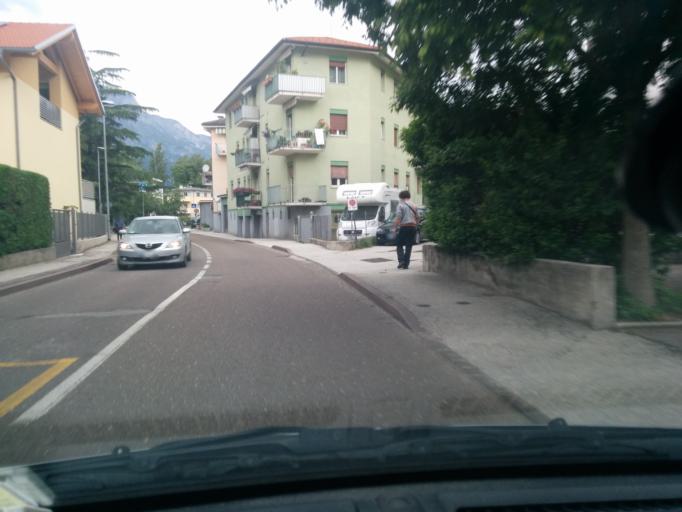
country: IT
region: Trentino-Alto Adige
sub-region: Provincia di Trento
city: Trento
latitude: 46.0856
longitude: 11.1225
